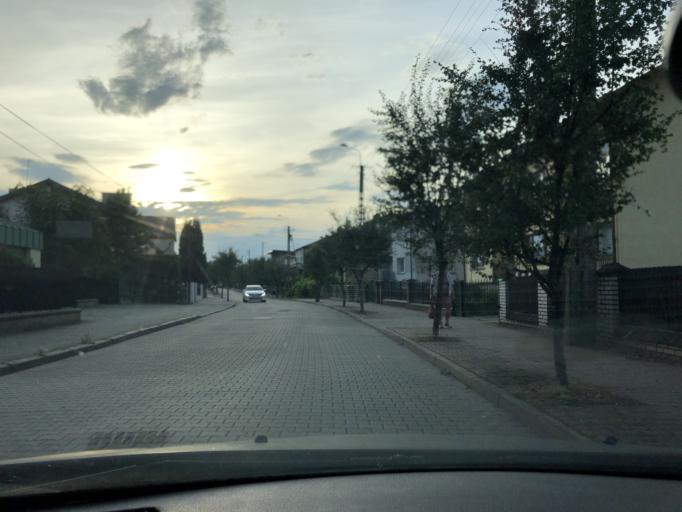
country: PL
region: Lodz Voivodeship
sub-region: Powiat wielunski
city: Wielun
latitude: 51.2224
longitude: 18.5671
